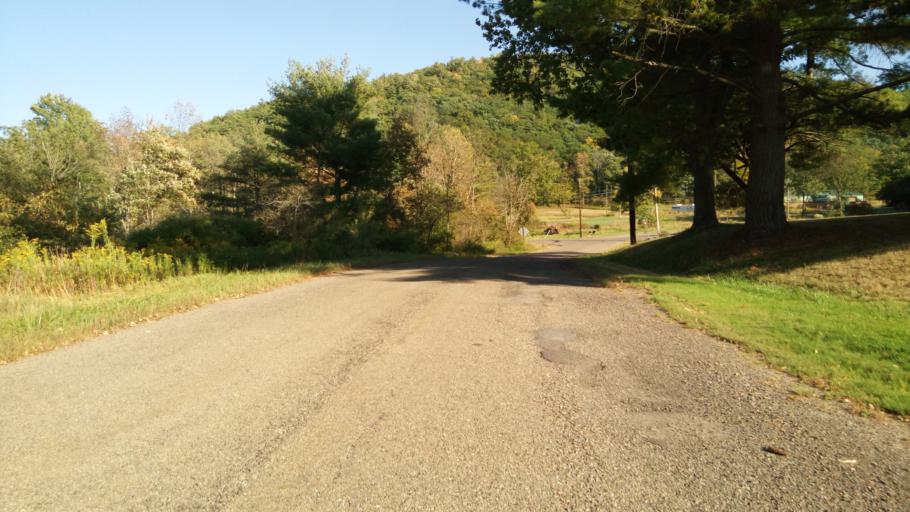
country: US
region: New York
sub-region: Chemung County
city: West Elmira
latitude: 42.0687
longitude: -76.8373
